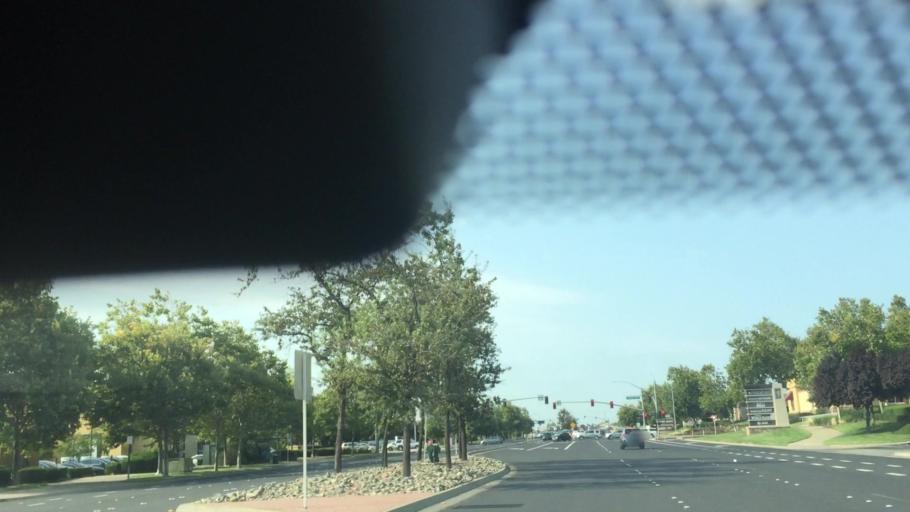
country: US
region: California
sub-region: Placer County
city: Roseville
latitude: 38.7706
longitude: -121.2657
